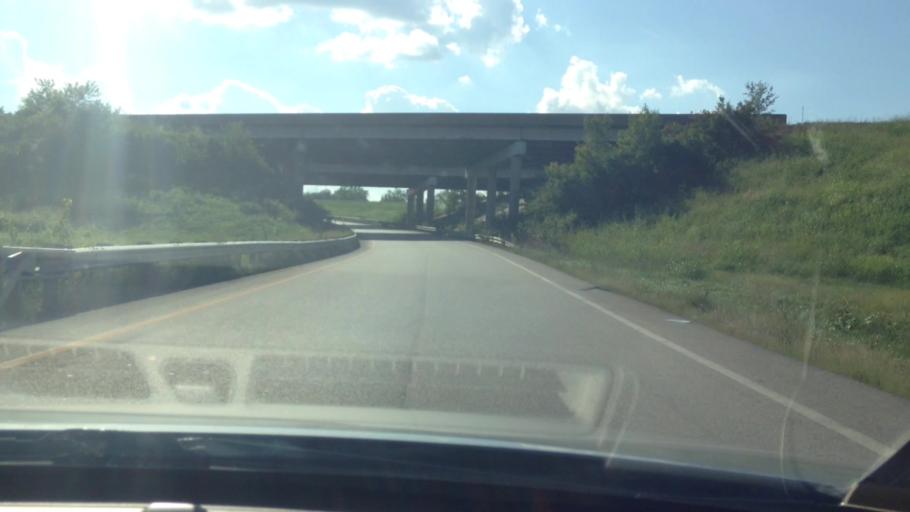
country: US
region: Missouri
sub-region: Clay County
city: Claycomo
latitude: 39.2076
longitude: -94.4897
